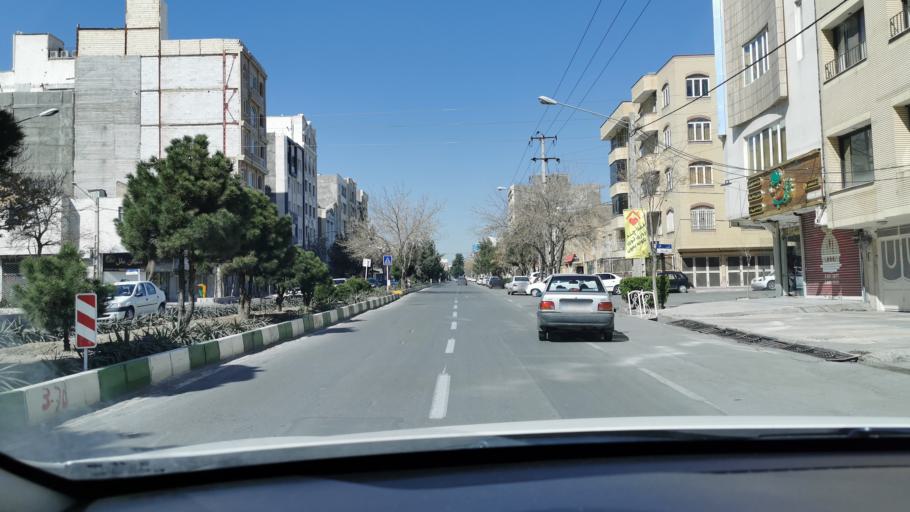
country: IR
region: Razavi Khorasan
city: Mashhad
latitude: 36.3259
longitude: 59.5221
